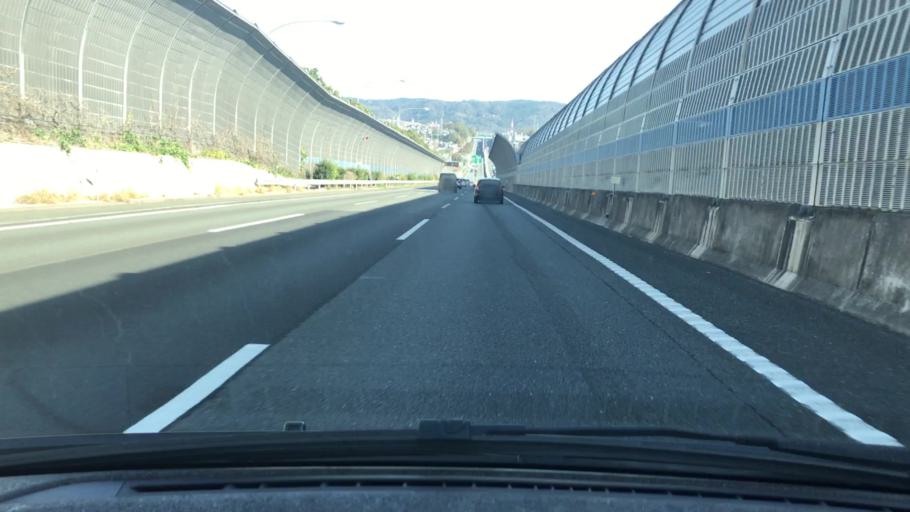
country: JP
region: Osaka
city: Takatsuki
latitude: 34.8570
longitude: 135.5940
